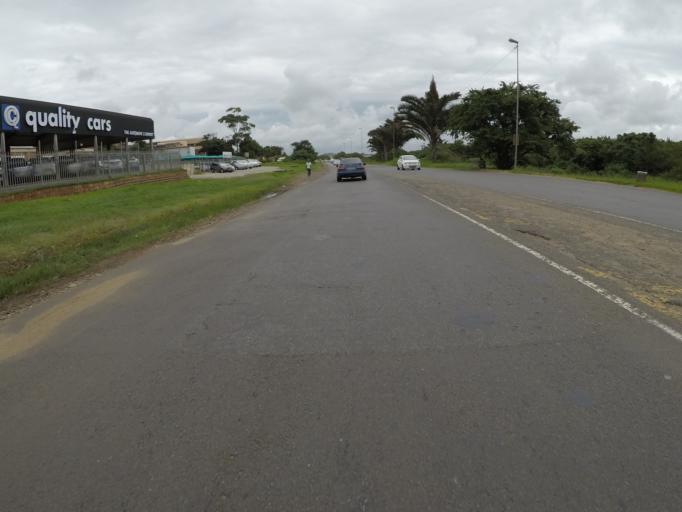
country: ZA
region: KwaZulu-Natal
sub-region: uThungulu District Municipality
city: Empangeni
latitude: -28.7648
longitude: 31.9066
